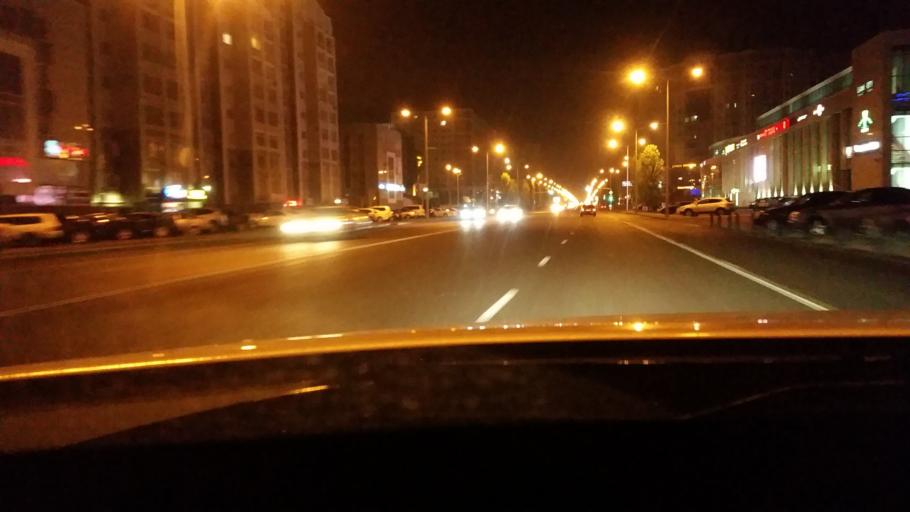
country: KZ
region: Astana Qalasy
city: Astana
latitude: 51.1387
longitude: 71.4739
